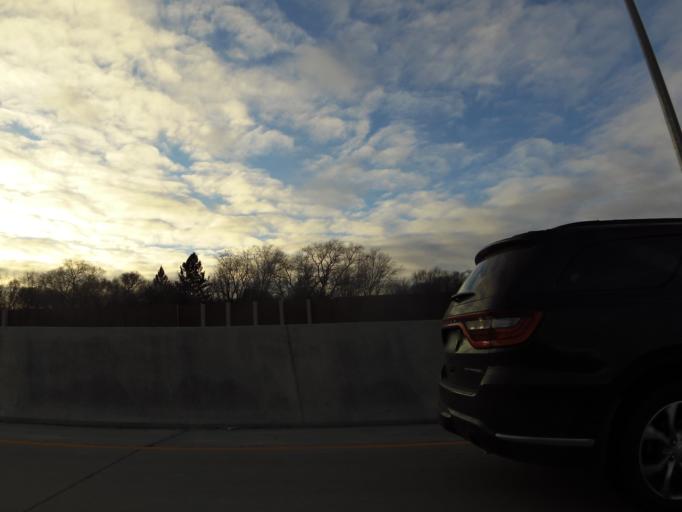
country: US
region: Minnesota
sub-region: Ramsey County
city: Vadnais Heights
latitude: 45.0604
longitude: -93.0567
